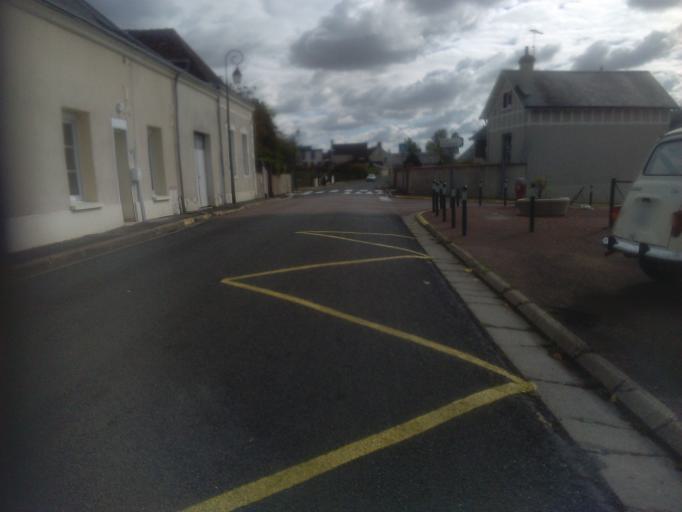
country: FR
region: Centre
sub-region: Departement du Loir-et-Cher
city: Villiers-sur-Loir
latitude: 47.8037
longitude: 0.9985
